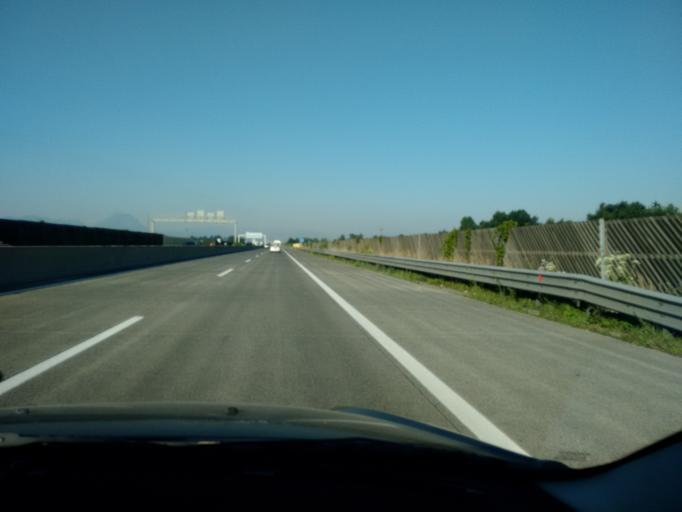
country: AT
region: Upper Austria
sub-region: Politischer Bezirk Gmunden
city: Vorchdorf
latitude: 48.0354
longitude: 13.9827
